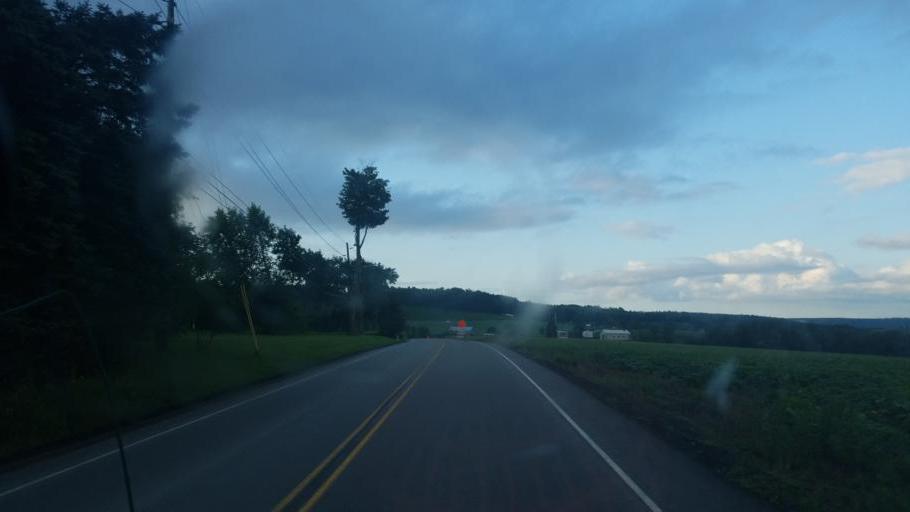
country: US
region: Pennsylvania
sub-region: Potter County
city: Galeton
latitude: 41.8605
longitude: -77.7666
